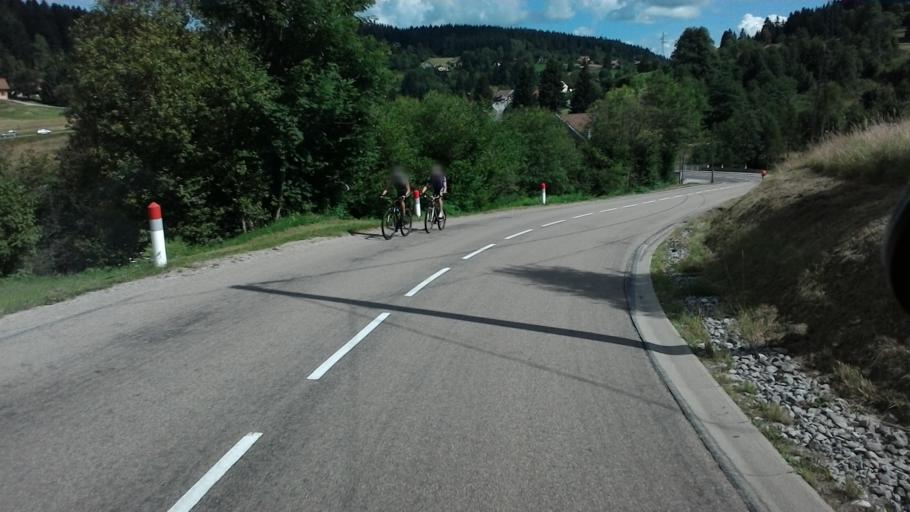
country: FR
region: Lorraine
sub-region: Departement des Vosges
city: Gerardmer
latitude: 48.0431
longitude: 6.8677
